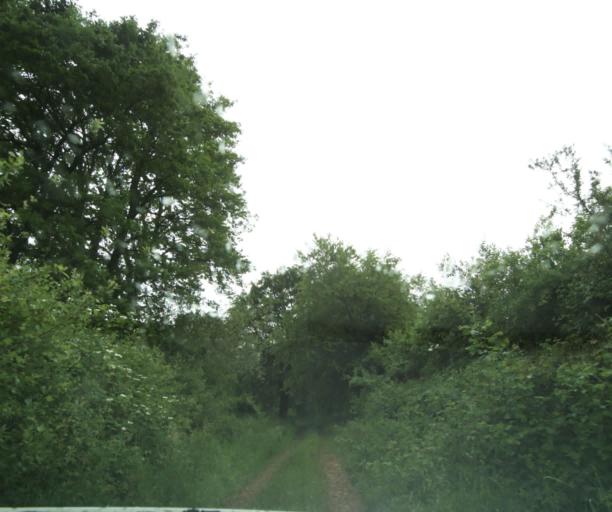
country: FR
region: Bourgogne
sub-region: Departement de Saone-et-Loire
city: Palinges
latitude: 46.5310
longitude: 4.2559
